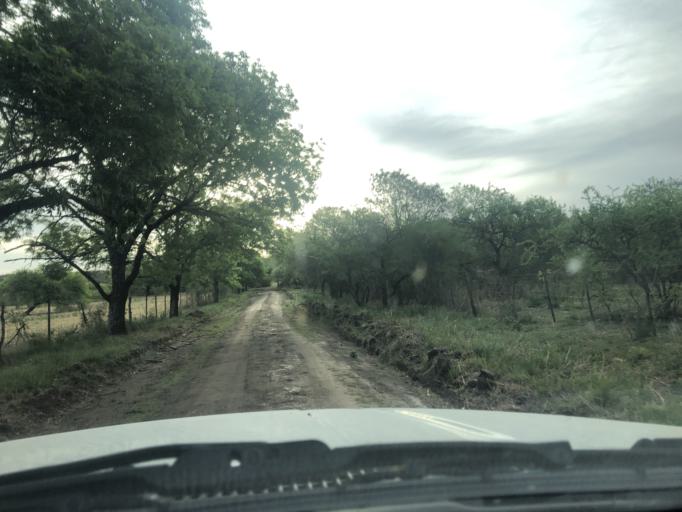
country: AR
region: Cordoba
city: La Granja
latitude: -31.0138
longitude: -64.2507
